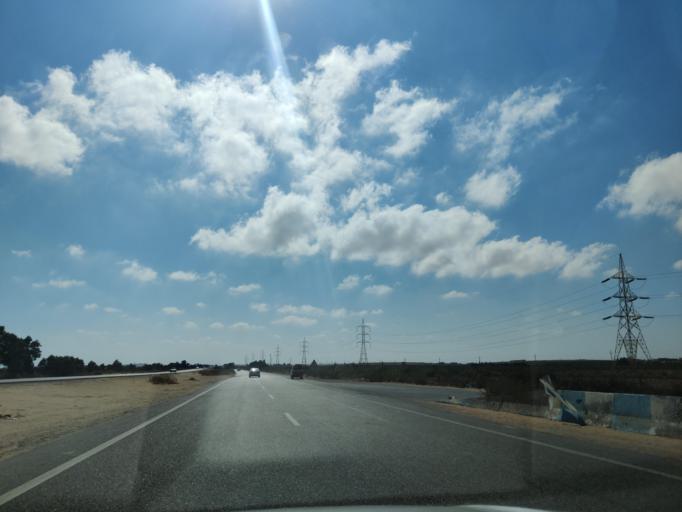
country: EG
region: Muhafazat Matruh
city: Al `Alamayn
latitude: 31.0540
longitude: 28.2913
